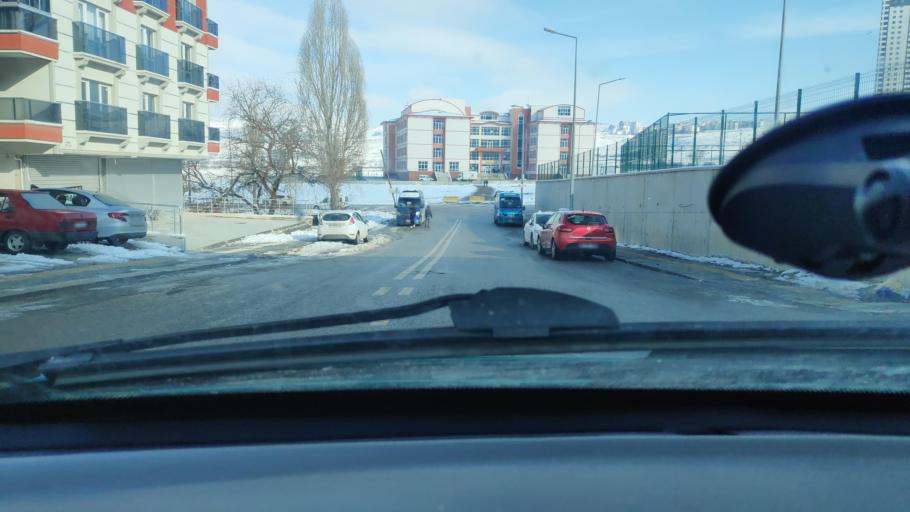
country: TR
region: Ankara
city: Ankara
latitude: 40.0136
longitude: 32.8438
